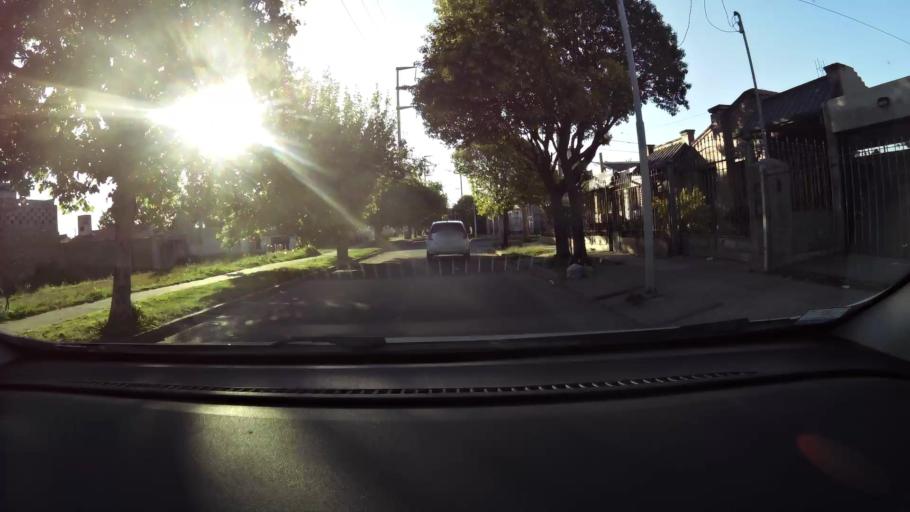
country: AR
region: Cordoba
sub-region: Departamento de Capital
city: Cordoba
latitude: -31.3728
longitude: -64.1972
